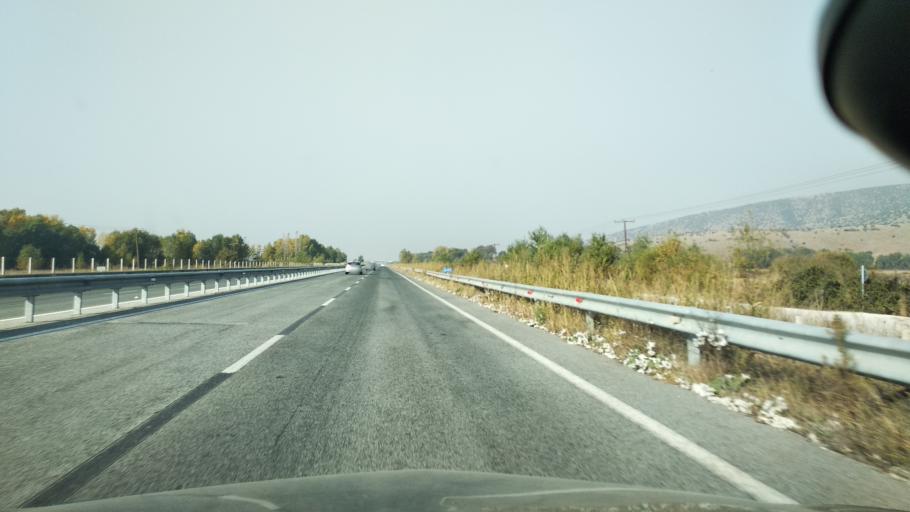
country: GR
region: Thessaly
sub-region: Trikala
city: Oichalia
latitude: 39.5646
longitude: 21.9518
